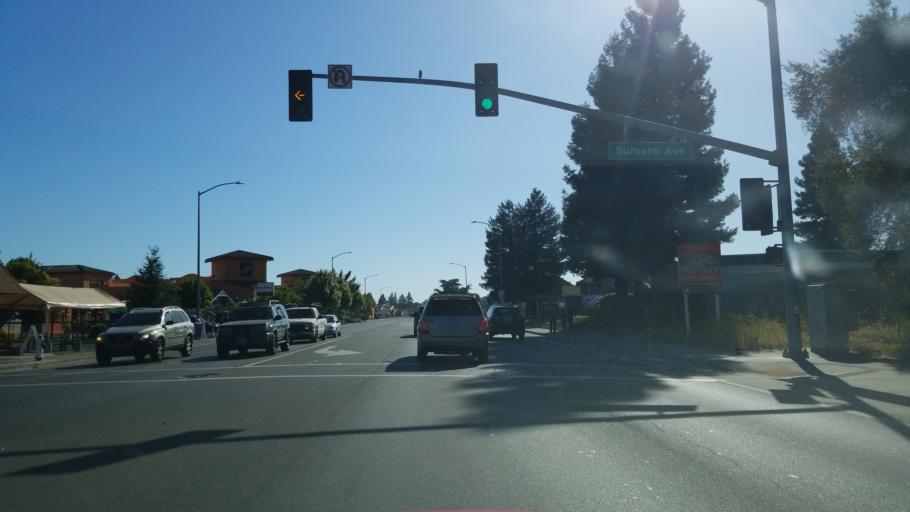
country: US
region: California
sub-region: Sonoma County
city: Roseland
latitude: 38.4283
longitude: -122.7353
